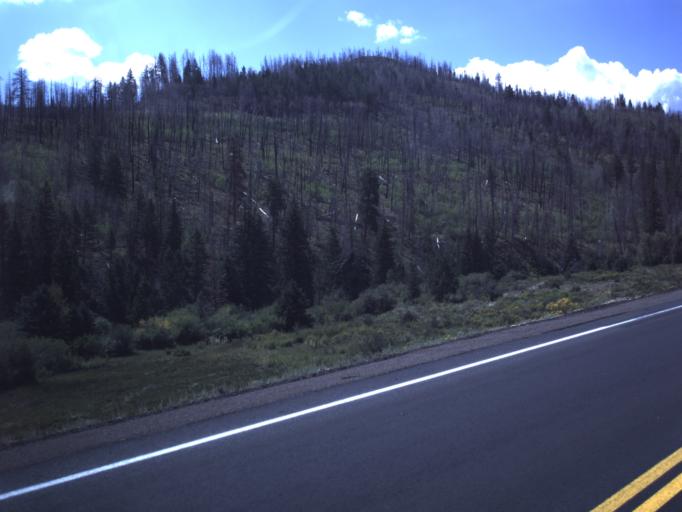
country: US
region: Utah
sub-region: Carbon County
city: Helper
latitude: 39.9170
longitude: -110.6902
